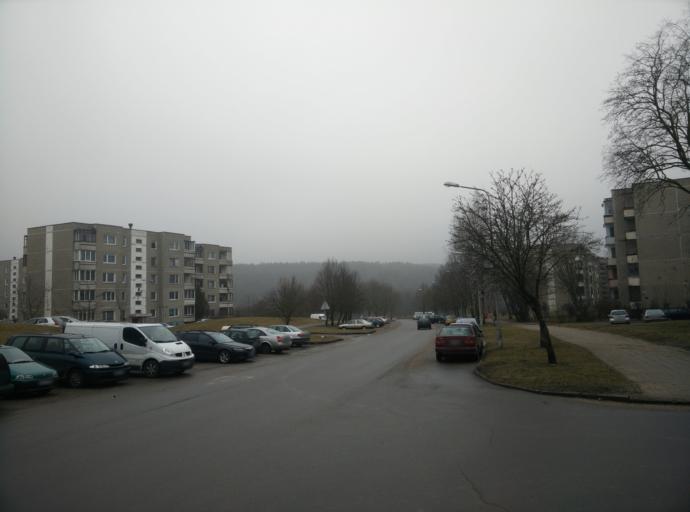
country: LT
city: Grigiskes
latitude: 54.6676
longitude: 25.0958
